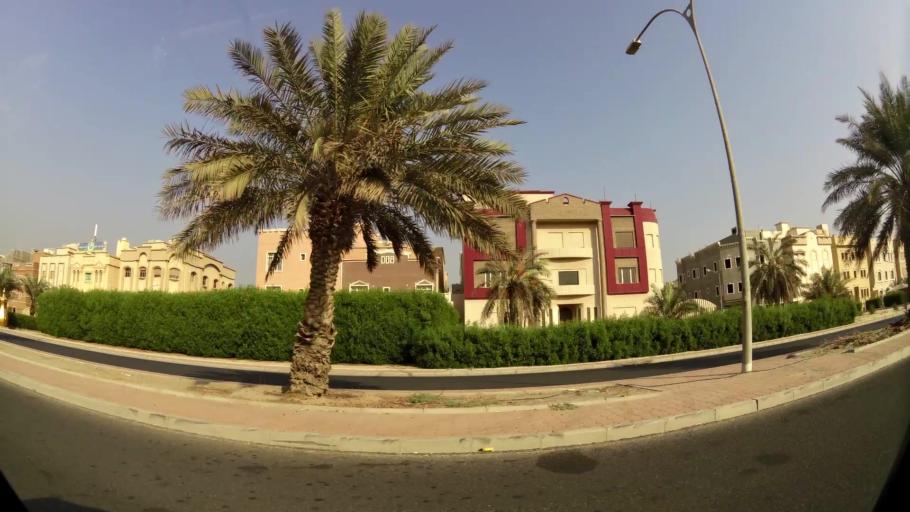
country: KW
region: Al Ahmadi
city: Ar Riqqah
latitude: 29.1246
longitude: 48.1045
